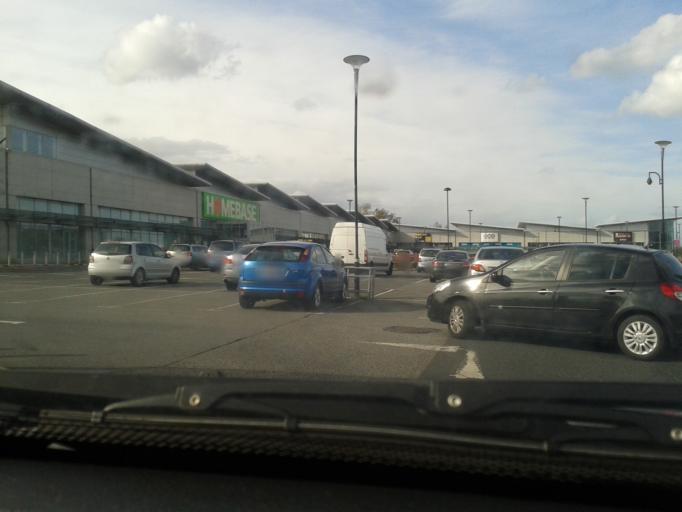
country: IE
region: Leinster
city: Ballymun
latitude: 53.4040
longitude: -6.2611
